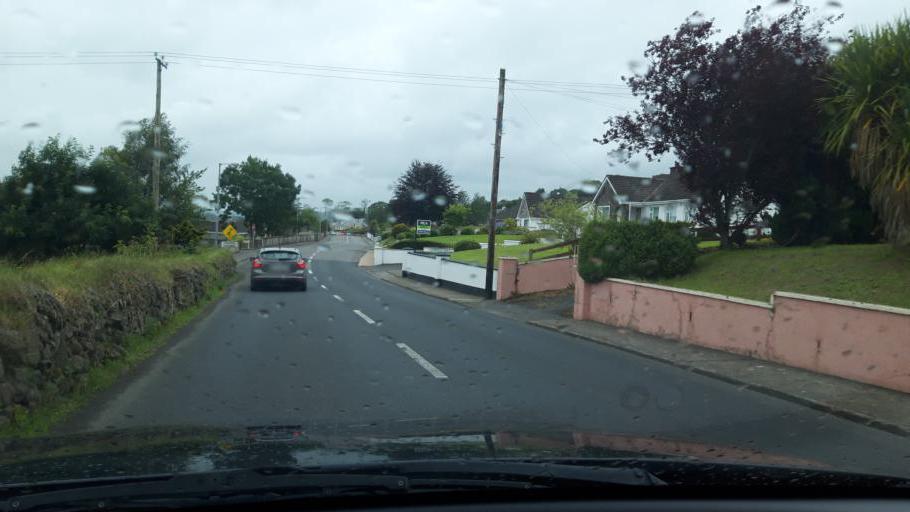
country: IE
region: Munster
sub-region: County Cork
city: Youghal
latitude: 52.1465
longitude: -7.8359
